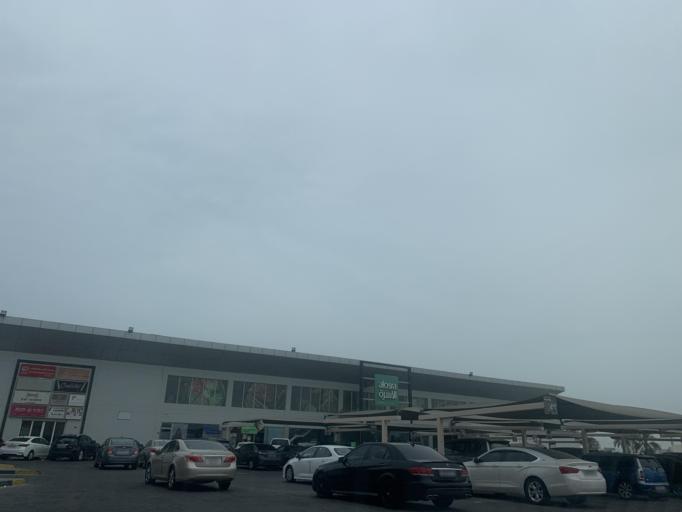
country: BH
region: Muharraq
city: Al Hadd
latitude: 26.2782
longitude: 50.6617
